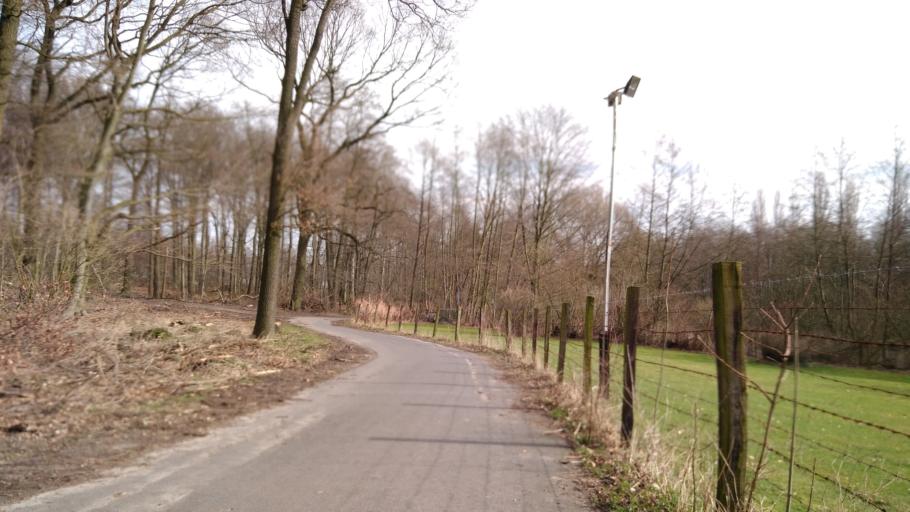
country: DE
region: North Rhine-Westphalia
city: Marl
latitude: 51.6125
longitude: 7.0815
